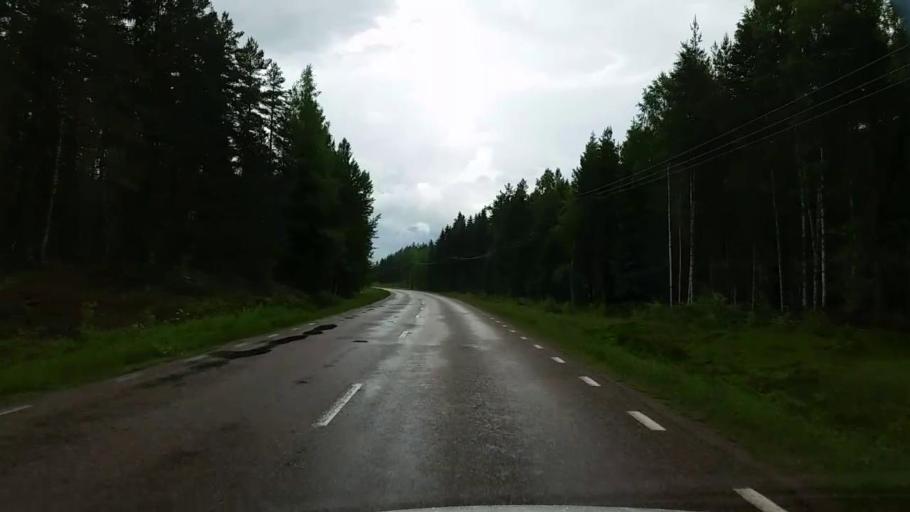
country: SE
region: Gaevleborg
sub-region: Sandvikens Kommun
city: Jarbo
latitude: 60.6696
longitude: 16.6183
